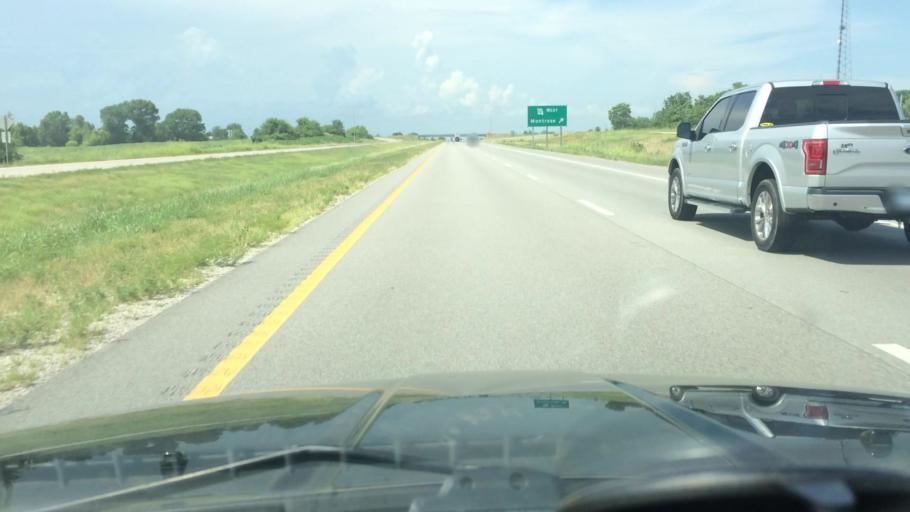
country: US
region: Missouri
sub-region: Henry County
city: Clinton
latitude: 38.2420
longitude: -93.7621
